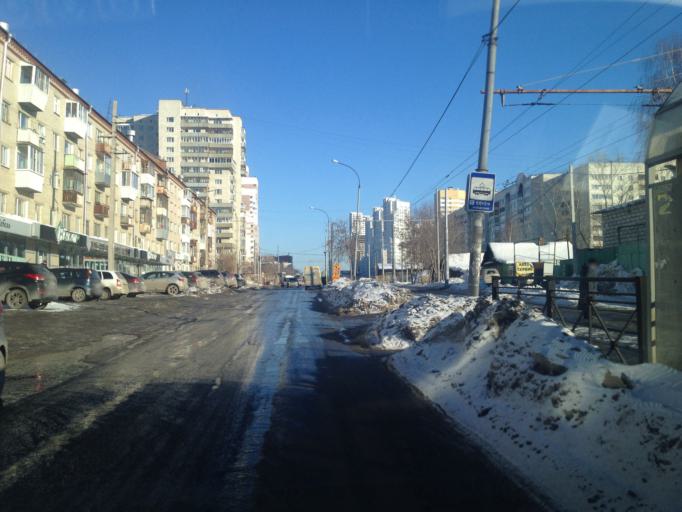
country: RU
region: Sverdlovsk
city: Yekaterinburg
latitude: 56.8360
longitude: 60.5537
